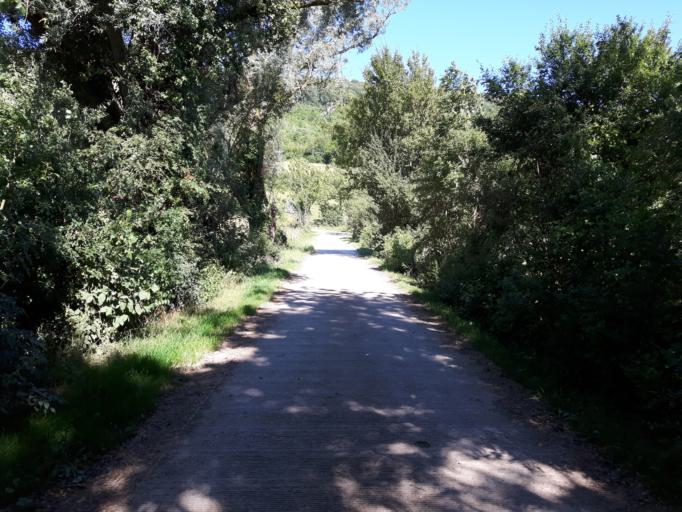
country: FR
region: Franche-Comte
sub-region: Departement du Jura
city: Mouchard
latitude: 47.0159
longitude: 5.8513
